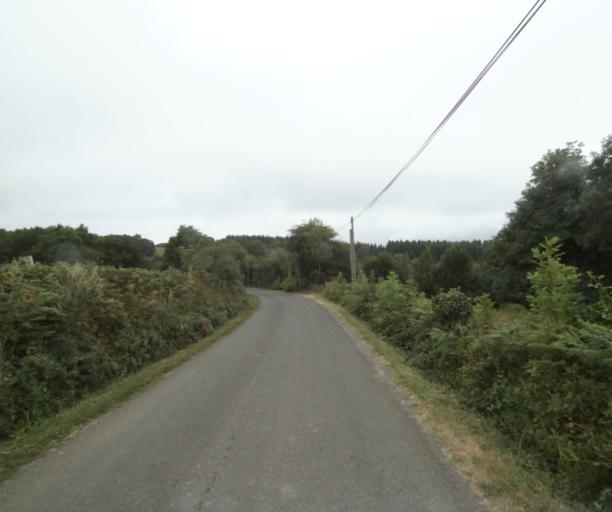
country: FR
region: Midi-Pyrenees
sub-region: Departement du Tarn
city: Soreze
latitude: 43.4090
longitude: 2.0559
